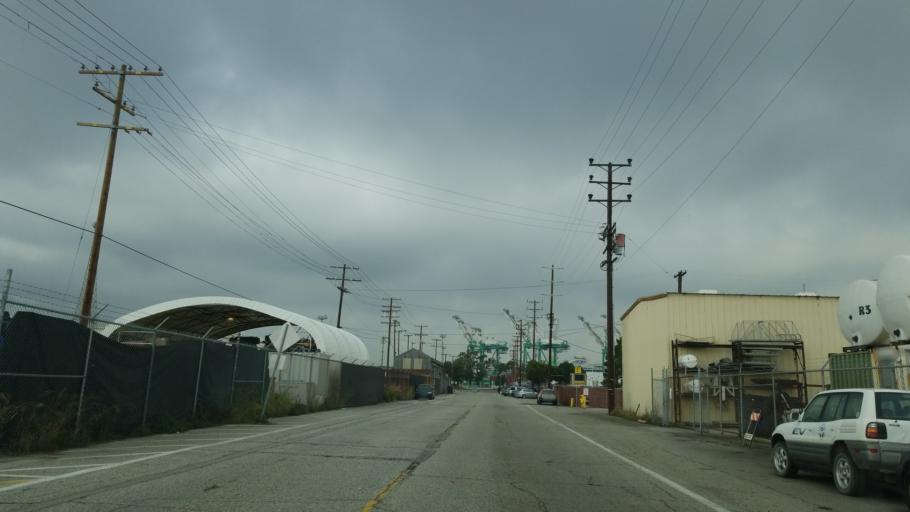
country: US
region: California
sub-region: Los Angeles County
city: San Pedro
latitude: 33.7352
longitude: -118.2700
